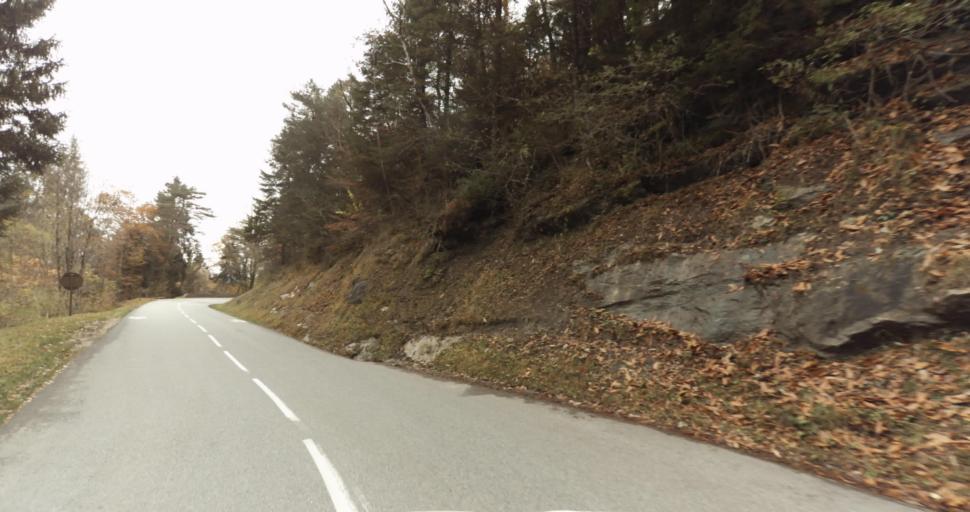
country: FR
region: Rhone-Alpes
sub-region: Departement de la Haute-Savoie
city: Sevrier
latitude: 45.8417
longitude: 6.1383
